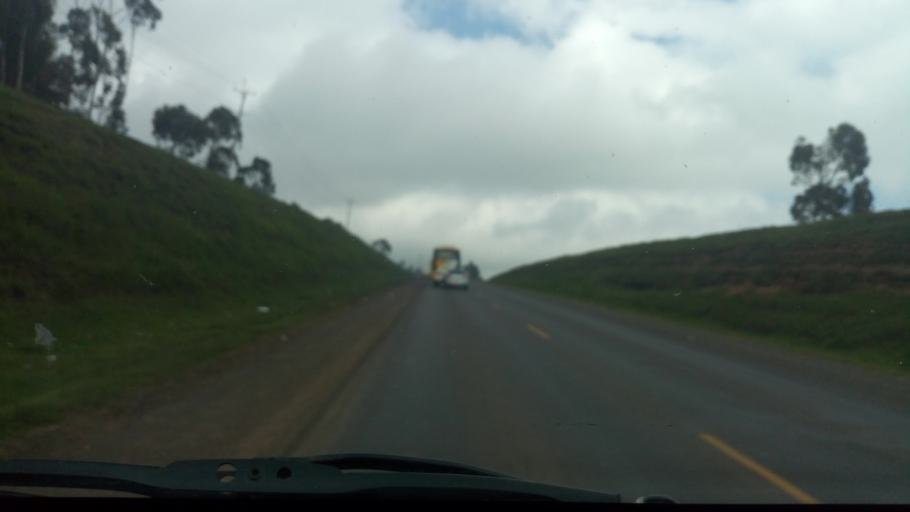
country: KE
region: Nakuru
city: Kijabe
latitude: -0.8425
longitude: 36.5501
